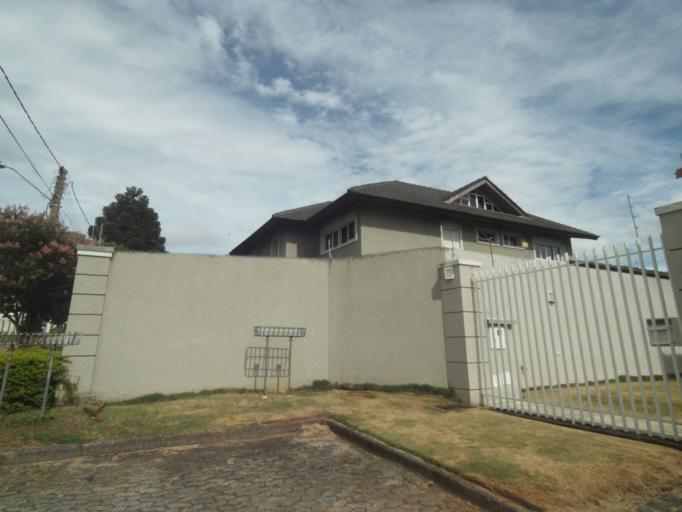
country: BR
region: Parana
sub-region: Curitiba
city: Curitiba
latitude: -25.4412
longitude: -49.3037
